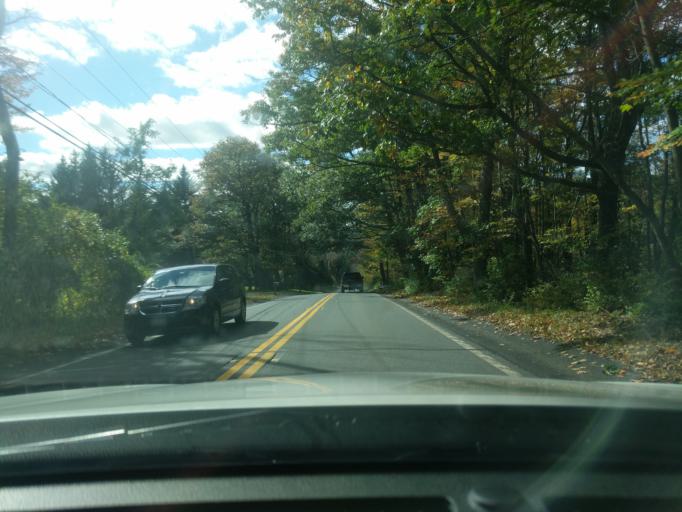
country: US
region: Massachusetts
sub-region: Hampden County
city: Granville
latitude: 42.1802
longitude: -72.9306
